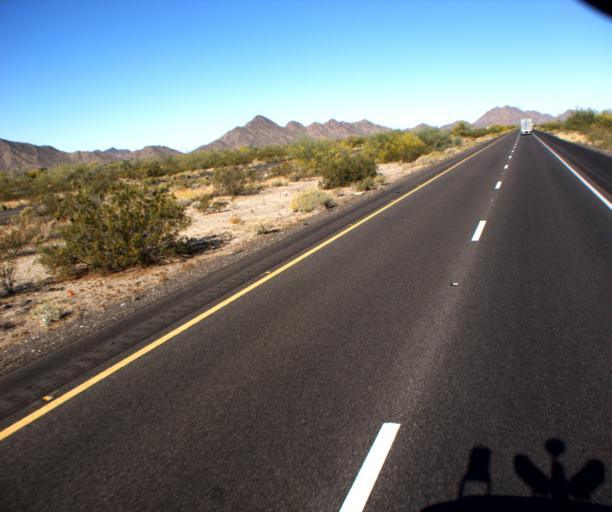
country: US
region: Arizona
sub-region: Maricopa County
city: Gila Bend
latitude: 32.8916
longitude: -112.4868
